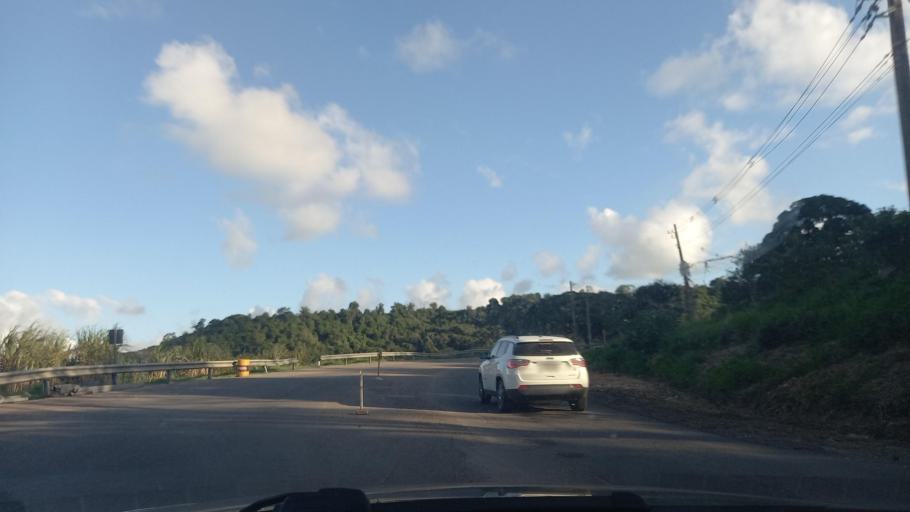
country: BR
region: Alagoas
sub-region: Sao Miguel Dos Campos
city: Sao Miguel dos Campos
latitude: -9.8187
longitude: -36.2191
